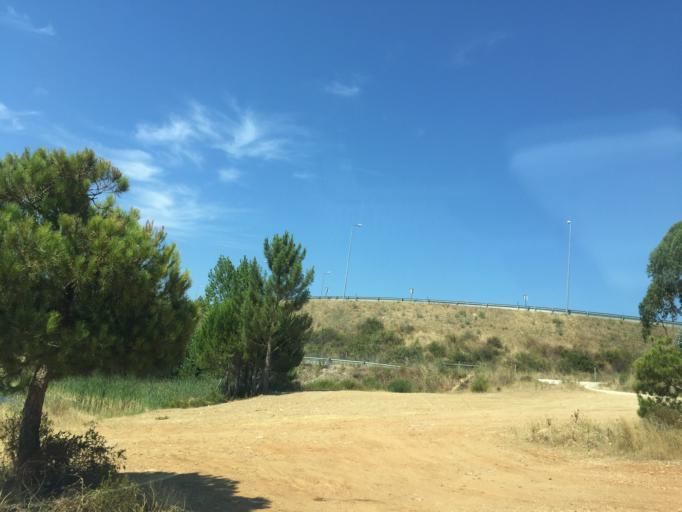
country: PT
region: Santarem
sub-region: Tomar
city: Tomar
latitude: 39.6163
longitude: -8.3603
